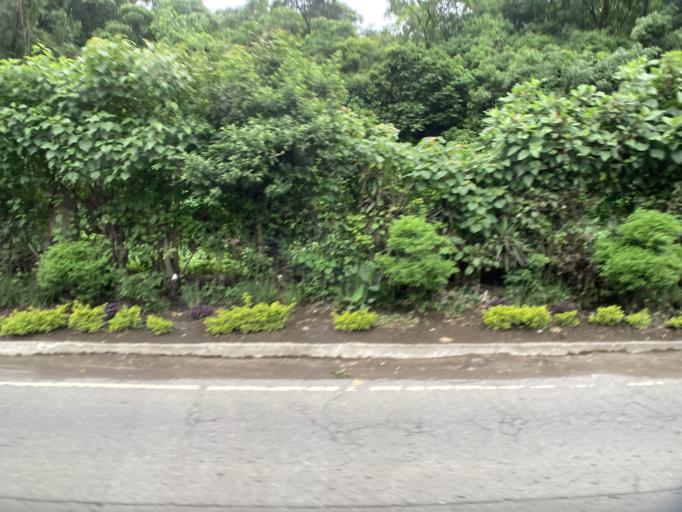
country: GT
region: Sacatepequez
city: Pastores
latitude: 14.6032
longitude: -90.7632
